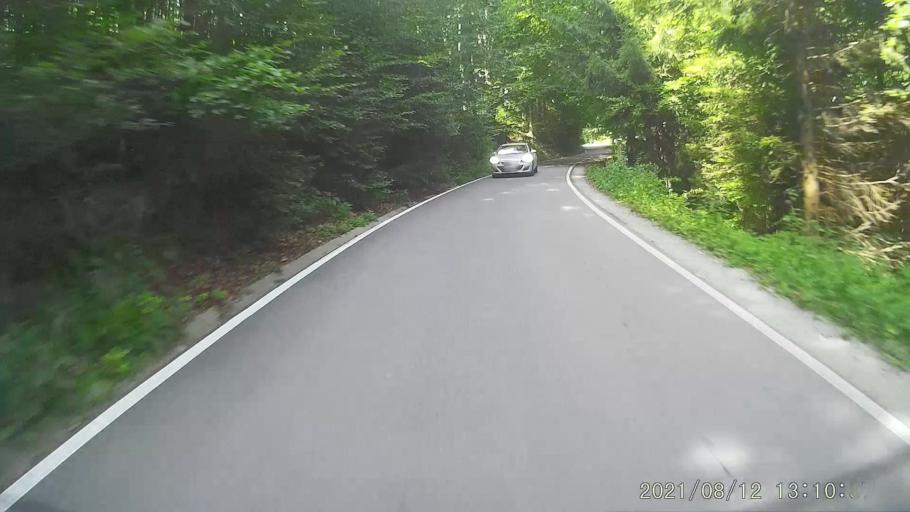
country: PL
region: Lower Silesian Voivodeship
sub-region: Powiat klodzki
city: Stronie Slaskie
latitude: 50.2462
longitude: 16.8490
